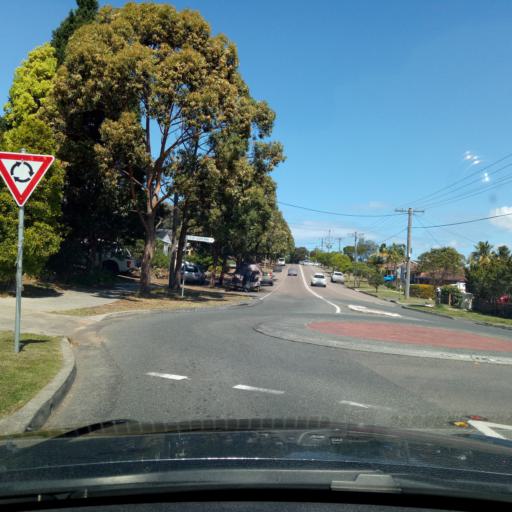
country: AU
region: New South Wales
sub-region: Wyong Shire
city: Bateau Bay
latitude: -33.3865
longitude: 151.4626
